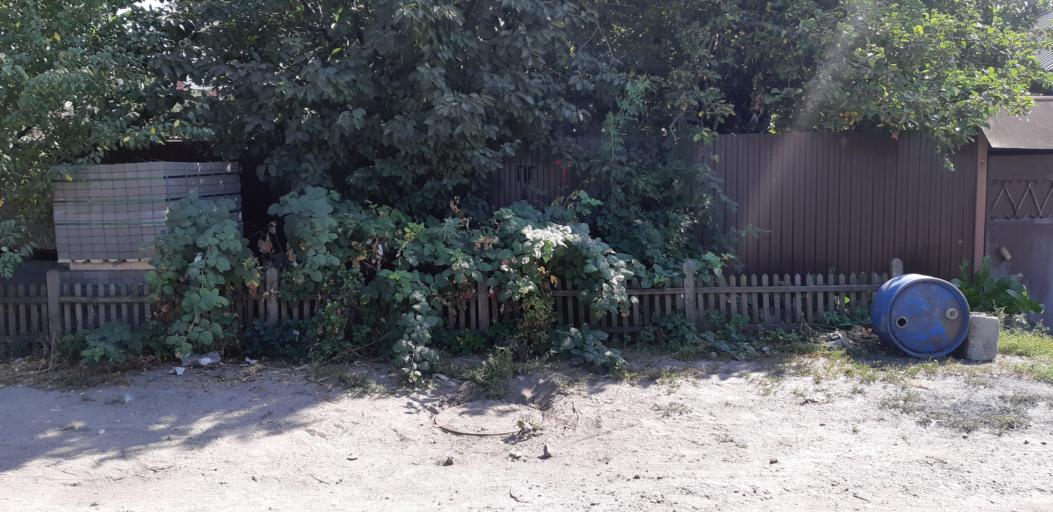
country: RU
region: Voronezj
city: Voronezh
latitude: 51.6647
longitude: 39.1700
